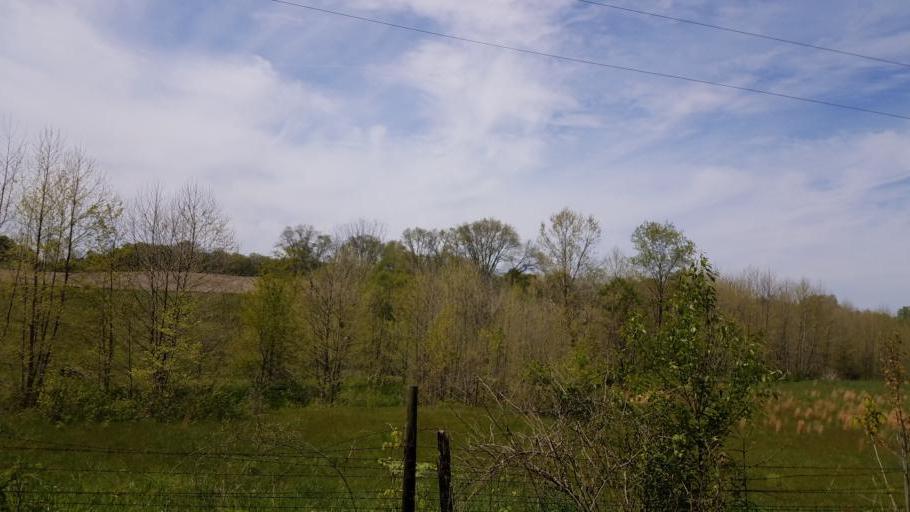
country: US
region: Ohio
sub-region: Knox County
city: Gambier
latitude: 40.3759
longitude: -82.3394
